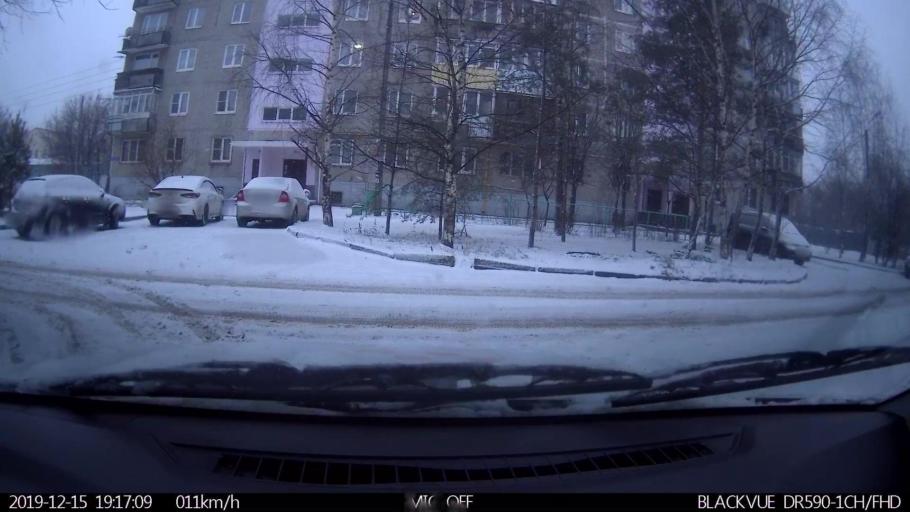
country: RU
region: Nizjnij Novgorod
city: Gorbatovka
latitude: 56.3512
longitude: 43.8436
